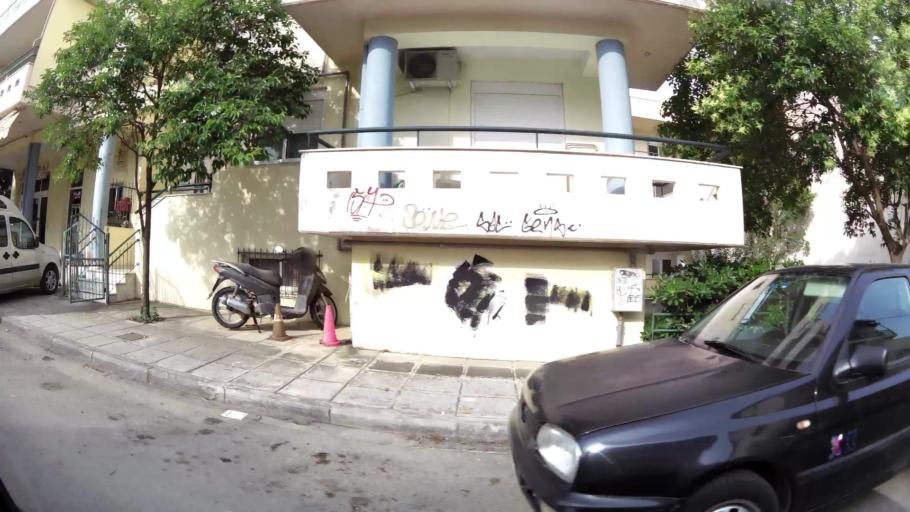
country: GR
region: Central Macedonia
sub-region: Nomos Thessalonikis
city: Thermi
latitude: 40.5460
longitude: 23.0183
